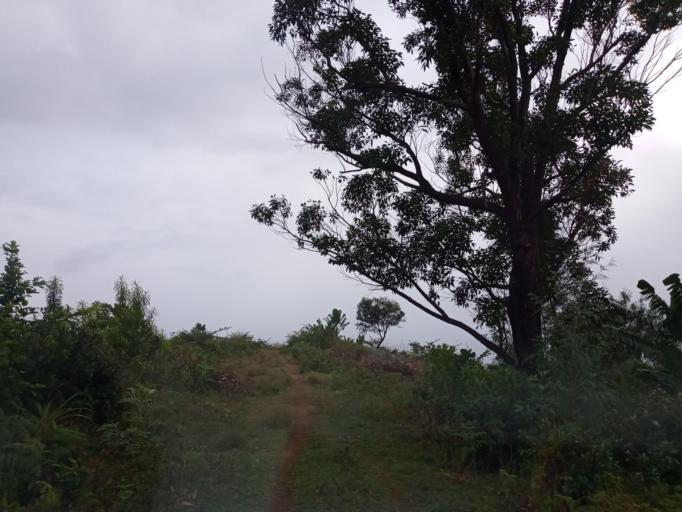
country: MG
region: Atsimo-Atsinanana
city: Vohipaho
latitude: -24.0118
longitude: 47.4153
